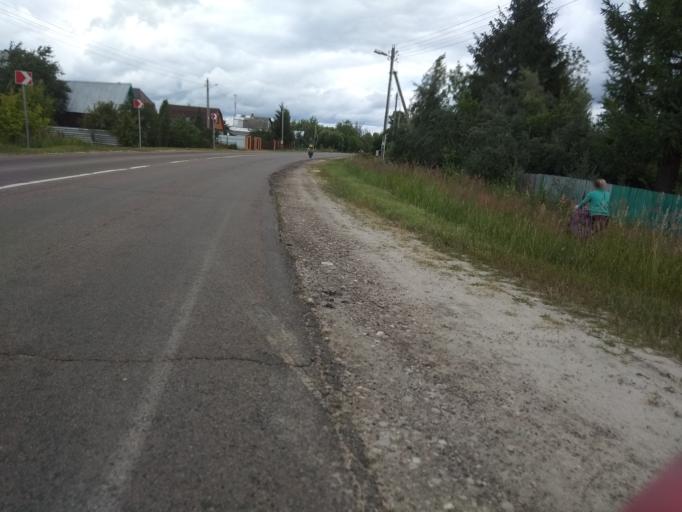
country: RU
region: Moskovskaya
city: Kerva
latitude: 55.5923
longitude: 39.7009
